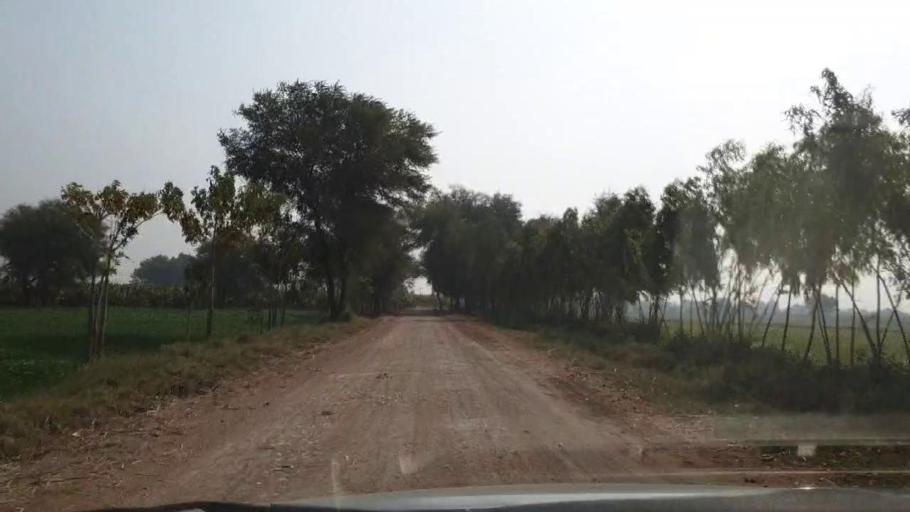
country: PK
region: Sindh
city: Matiari
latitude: 25.6563
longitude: 68.5498
